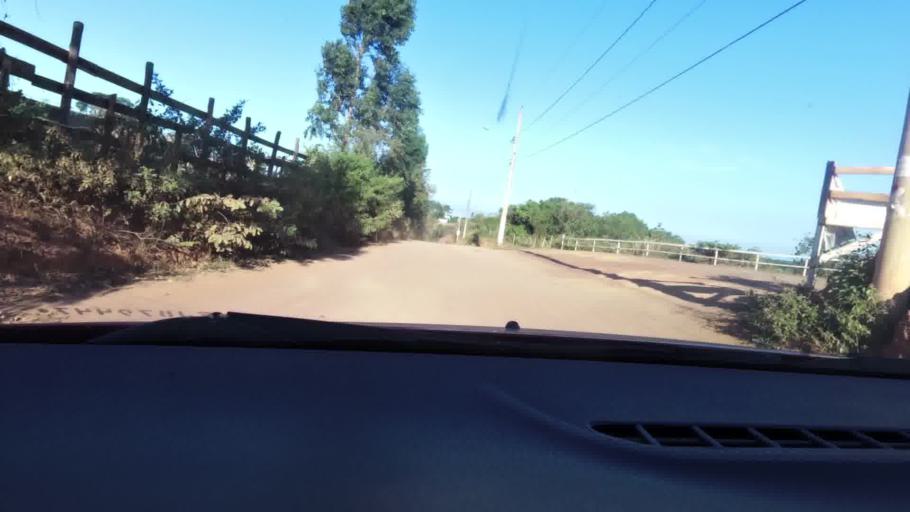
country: BR
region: Espirito Santo
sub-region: Guarapari
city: Guarapari
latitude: -20.5514
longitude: -40.4206
